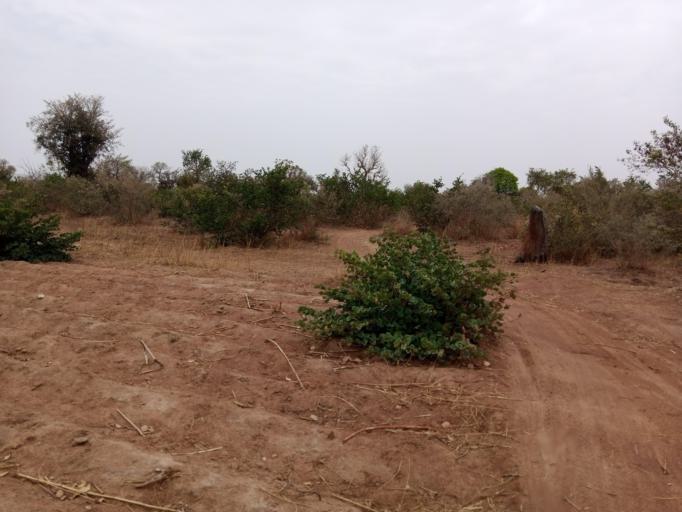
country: BF
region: Boucle du Mouhoun
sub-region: Province de la Kossi
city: Nouna
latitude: 12.8469
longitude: -4.0779
